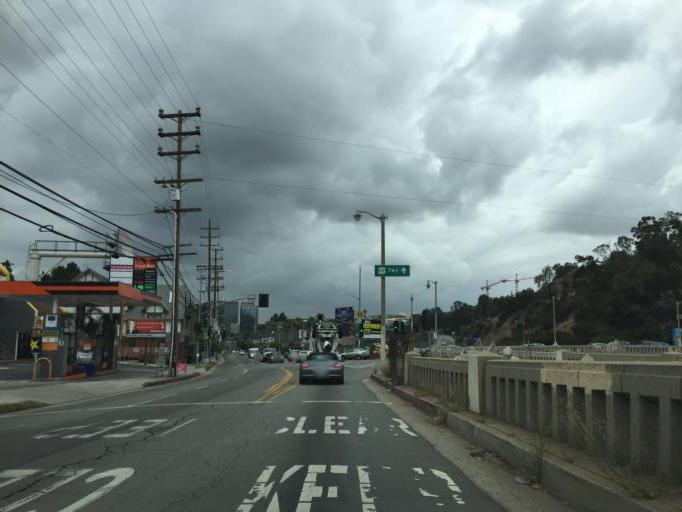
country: US
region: California
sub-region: Los Angeles County
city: Universal City
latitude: 34.1280
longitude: -118.3467
